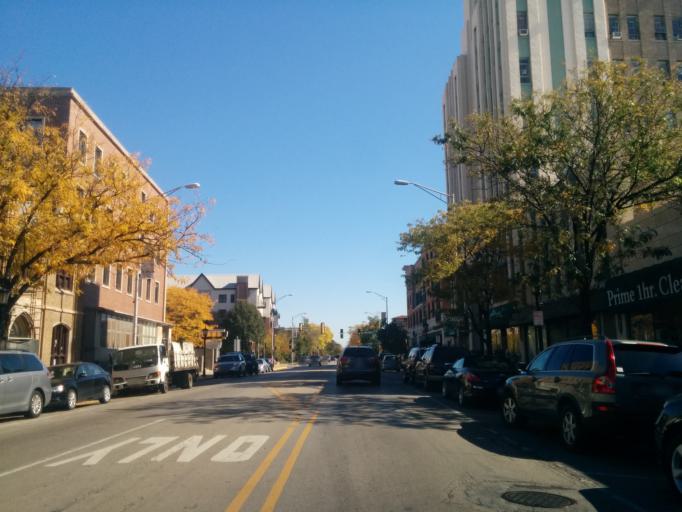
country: US
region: Illinois
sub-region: Cook County
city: Oak Park
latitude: 41.8886
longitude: -87.7941
